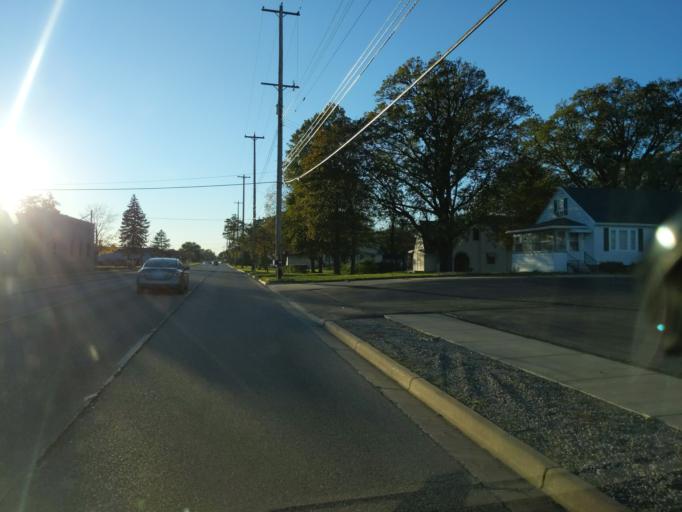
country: US
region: Michigan
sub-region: Ingham County
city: Edgemont Park
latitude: 42.7266
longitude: -84.5963
